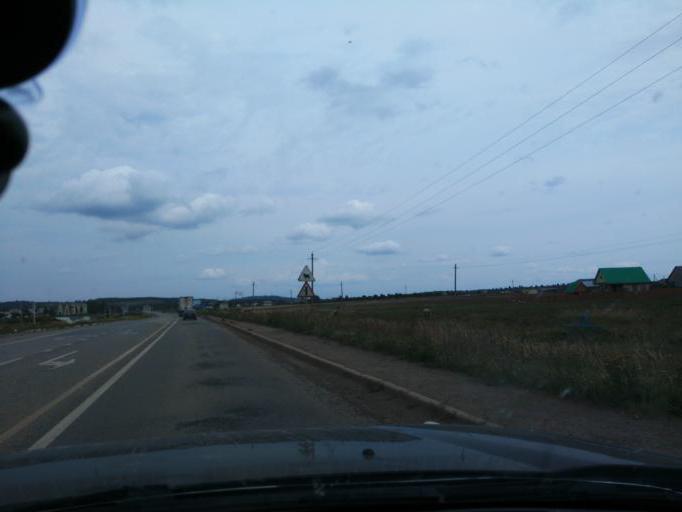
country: RU
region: Perm
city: Kuyeda
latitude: 56.4490
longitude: 55.6019
